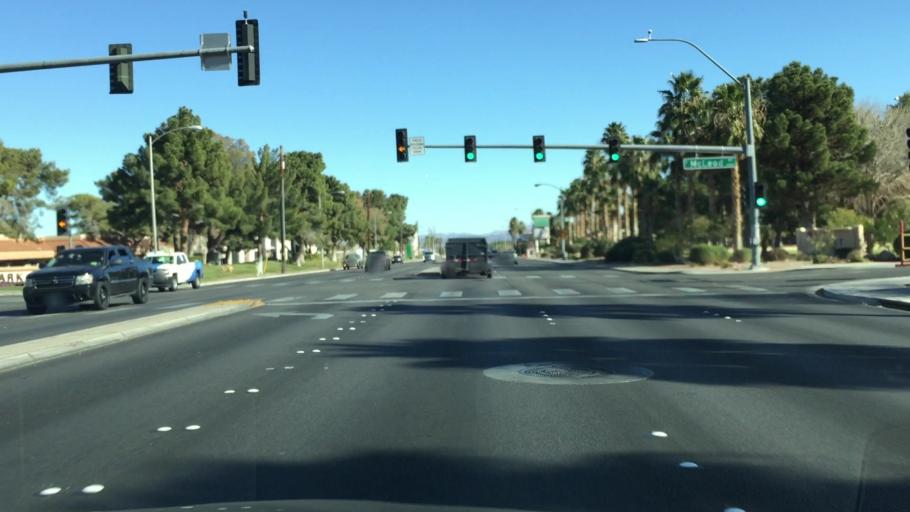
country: US
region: Nevada
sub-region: Clark County
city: Whitney
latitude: 36.0715
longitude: -115.1131
